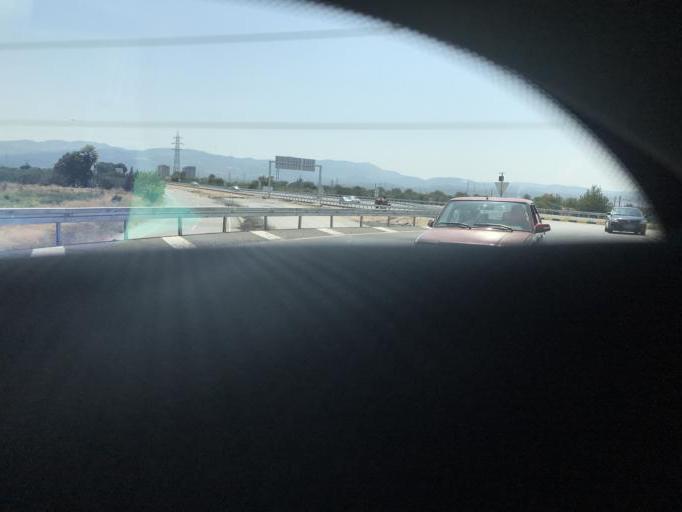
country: TR
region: Manisa
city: Akhisar
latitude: 38.9540
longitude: 27.8211
